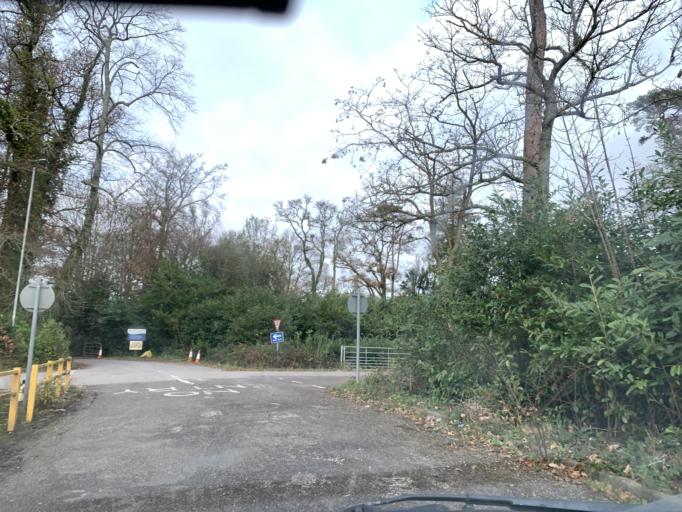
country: GB
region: England
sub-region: Hampshire
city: Cadnam
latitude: 50.9065
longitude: -1.6126
